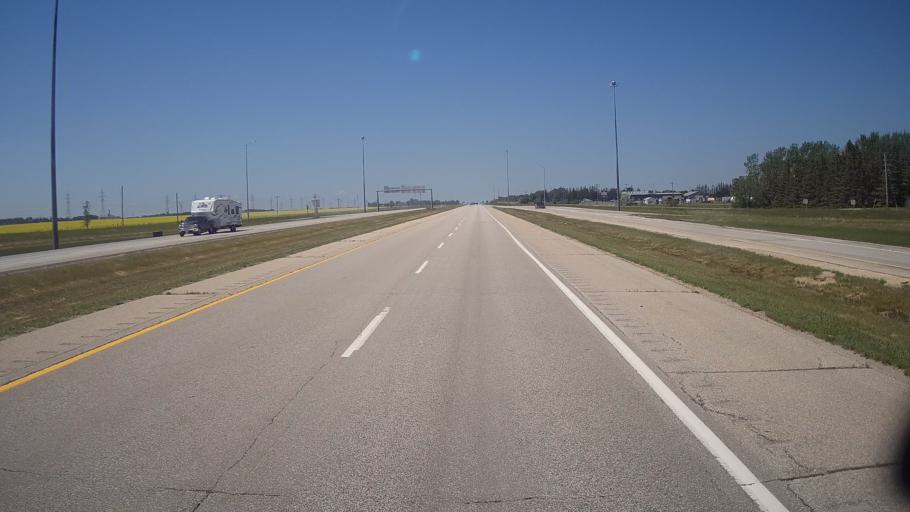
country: CA
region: Manitoba
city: Winnipeg
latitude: 49.9900
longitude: -97.2332
